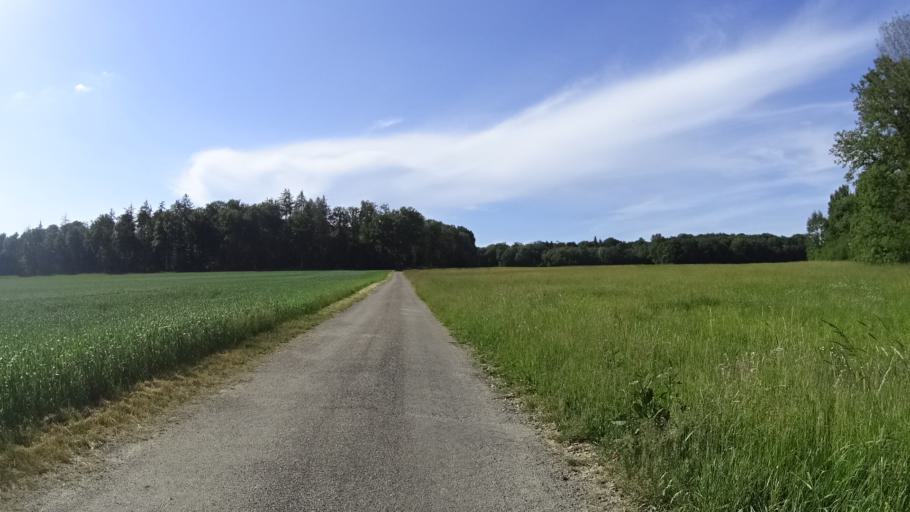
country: DE
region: Baden-Wuerttemberg
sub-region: Regierungsbezirk Stuttgart
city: Buch am Ahorn
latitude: 49.5280
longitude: 9.5429
